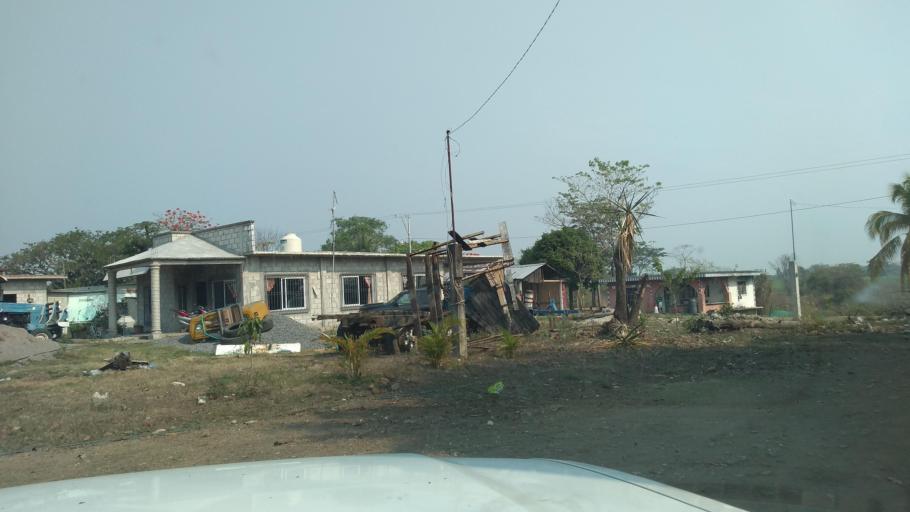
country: MX
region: Oaxaca
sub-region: Cosolapa
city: Cosolapa
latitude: 18.6250
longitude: -96.6047
